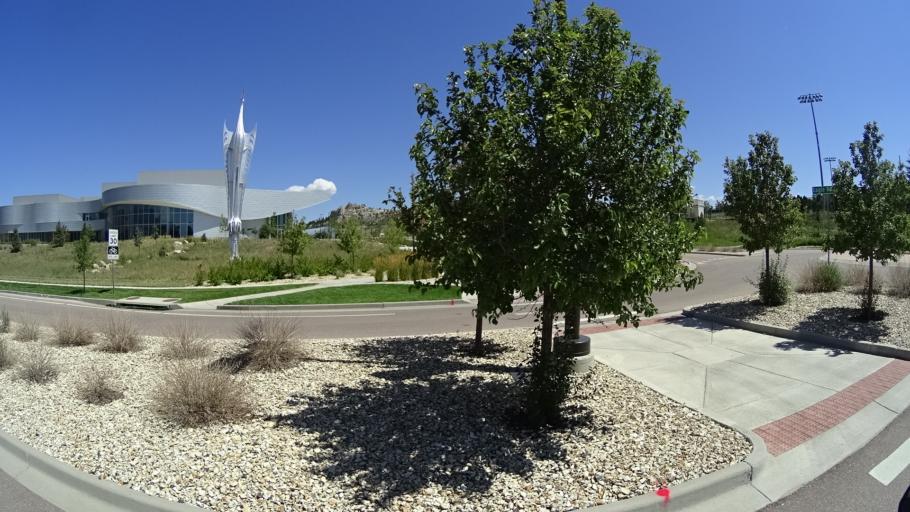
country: US
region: Colorado
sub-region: El Paso County
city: Colorado Springs
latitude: 38.9033
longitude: -104.8148
